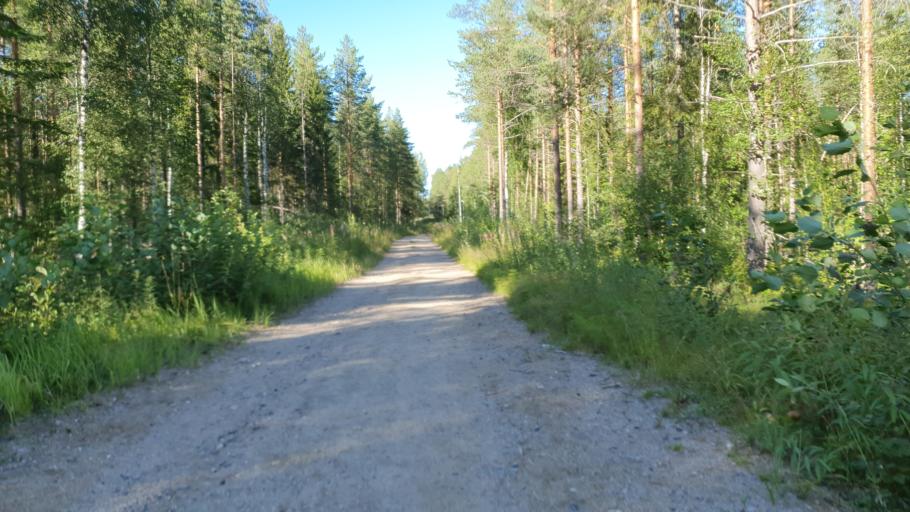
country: FI
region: Kainuu
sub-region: Kehys-Kainuu
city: Kuhmo
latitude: 64.1116
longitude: 29.5143
